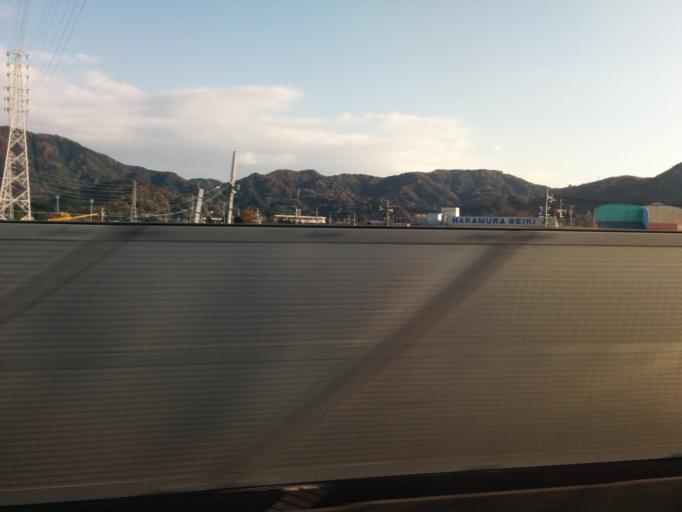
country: JP
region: Aichi
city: Gamagori
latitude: 34.8226
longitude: 137.2465
